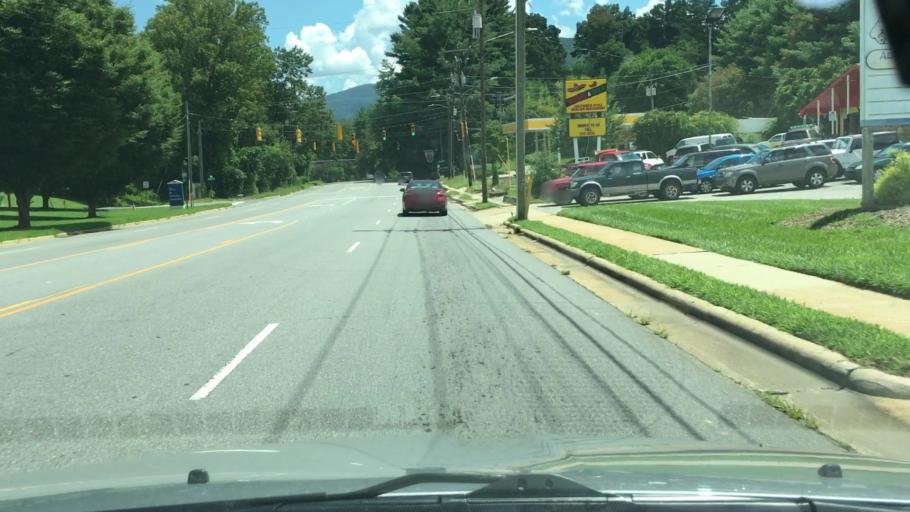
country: US
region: North Carolina
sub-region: Buncombe County
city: Biltmore Forest
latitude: 35.5868
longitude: -82.4834
